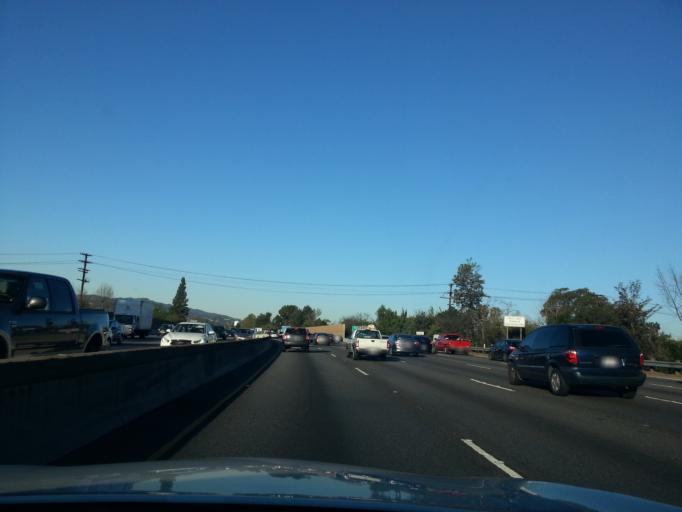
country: US
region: California
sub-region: Los Angeles County
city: Sherman Oaks
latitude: 34.1568
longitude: -118.4212
